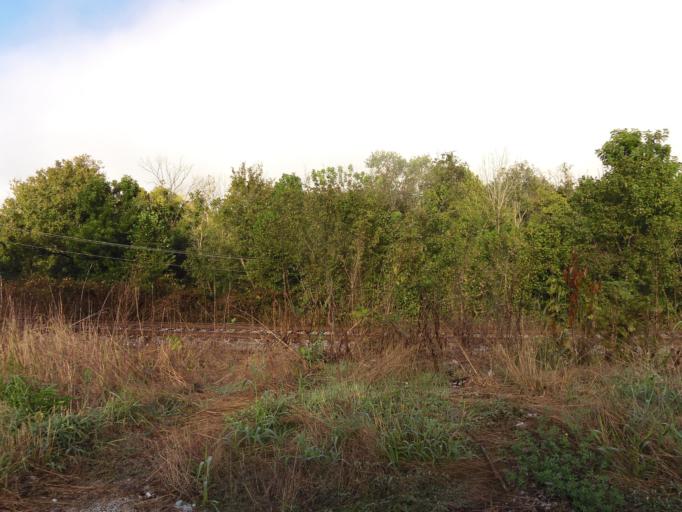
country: US
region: Tennessee
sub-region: Campbell County
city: Jellico
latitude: 36.5936
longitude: -84.1265
